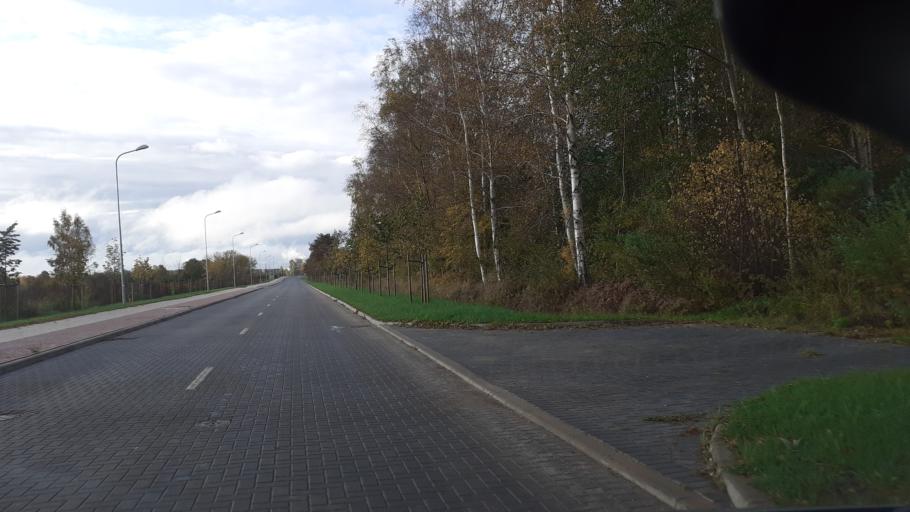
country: LV
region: Kuldigas Rajons
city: Kuldiga
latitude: 56.9848
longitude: 21.9493
